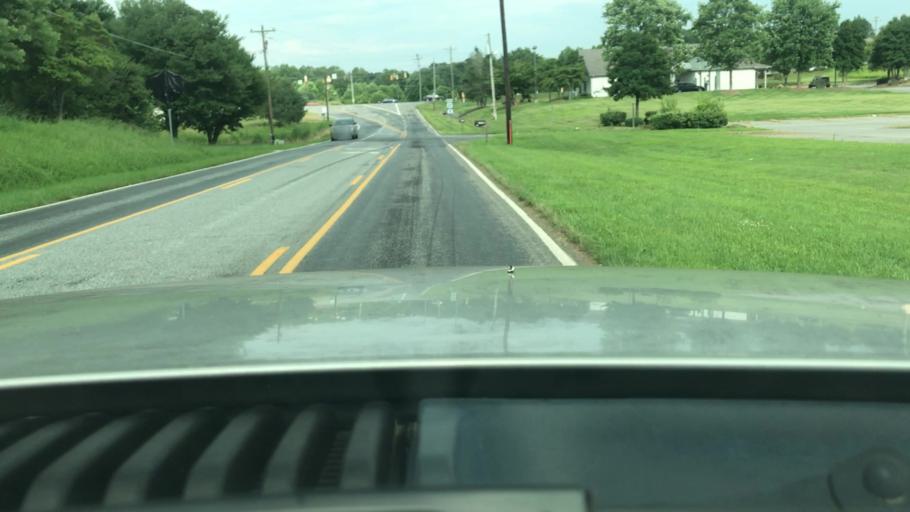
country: US
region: North Carolina
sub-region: Surry County
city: Elkin
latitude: 36.2885
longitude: -80.8549
